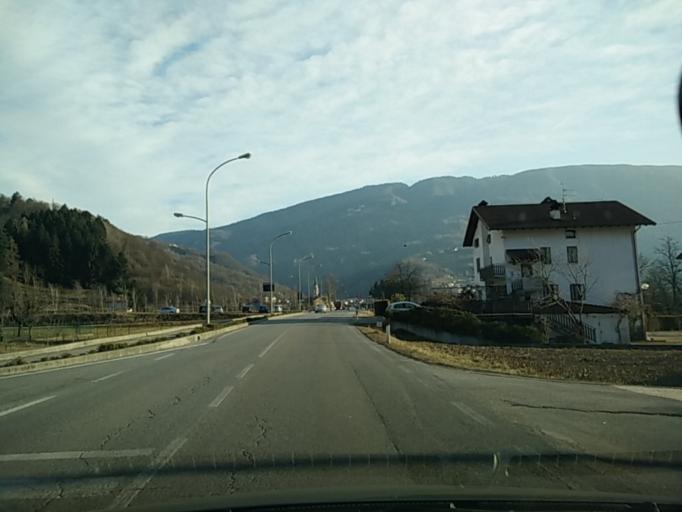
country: IT
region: Veneto
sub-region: Provincia di Belluno
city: Farra d'Alpago
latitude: 46.1264
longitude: 12.3521
